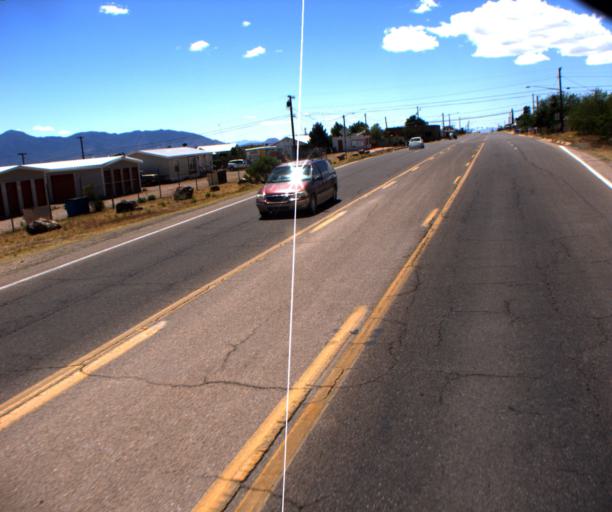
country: US
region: Arizona
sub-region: Cochise County
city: Bisbee
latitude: 31.4041
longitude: -109.9127
